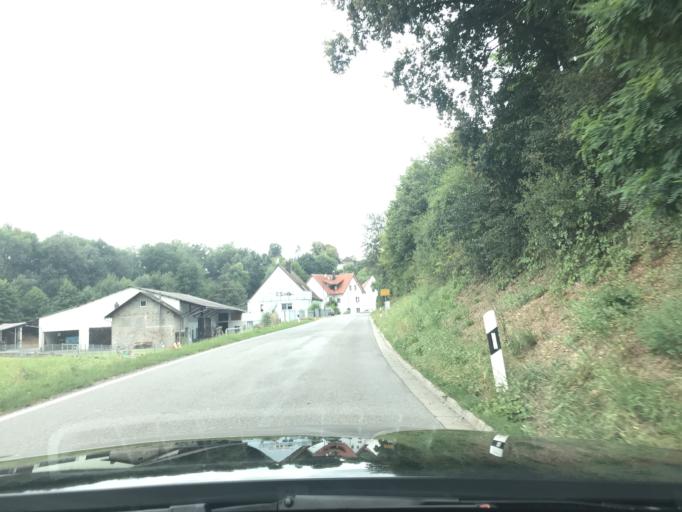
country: DE
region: Bavaria
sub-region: Regierungsbezirk Unterfranken
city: Breitbrunn
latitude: 50.0420
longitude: 10.6616
